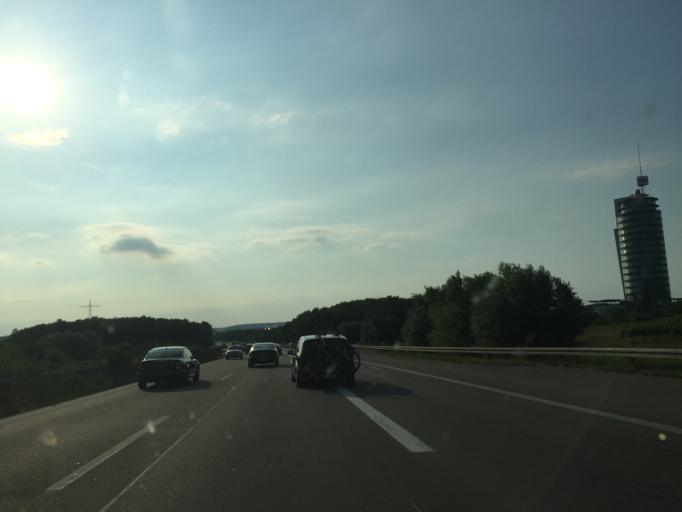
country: DE
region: Baden-Wuerttemberg
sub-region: Regierungsbezirk Stuttgart
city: Neckarsulm
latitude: 49.1788
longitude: 9.2346
